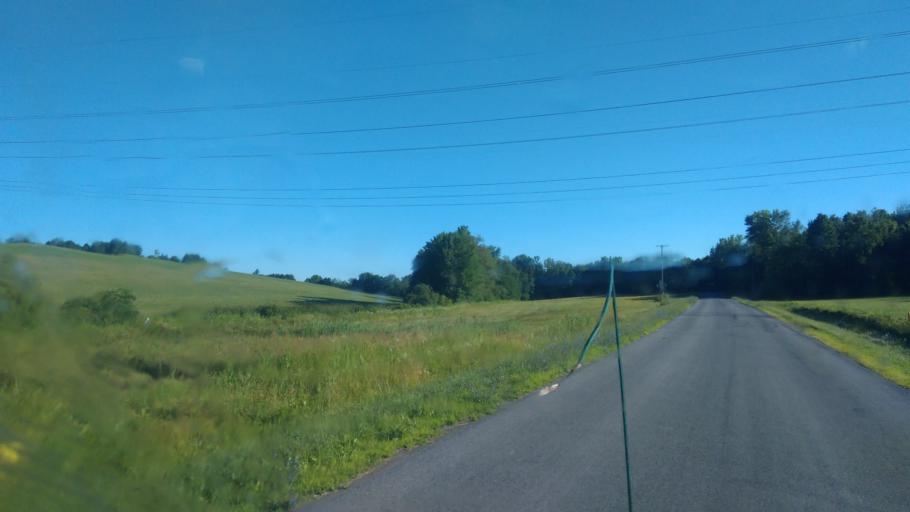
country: US
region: New York
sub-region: Wayne County
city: Lyons
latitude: 43.1309
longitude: -77.0381
